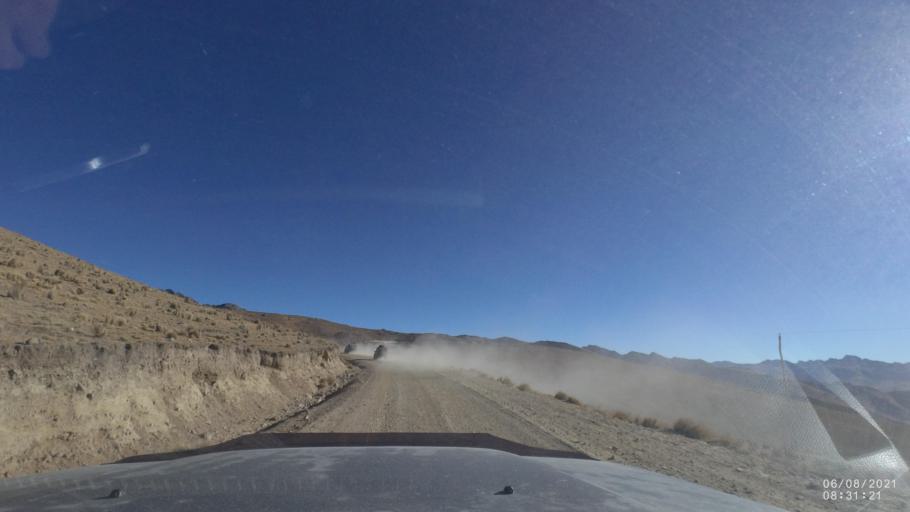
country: BO
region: Cochabamba
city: Sipe Sipe
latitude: -17.1868
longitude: -66.3724
